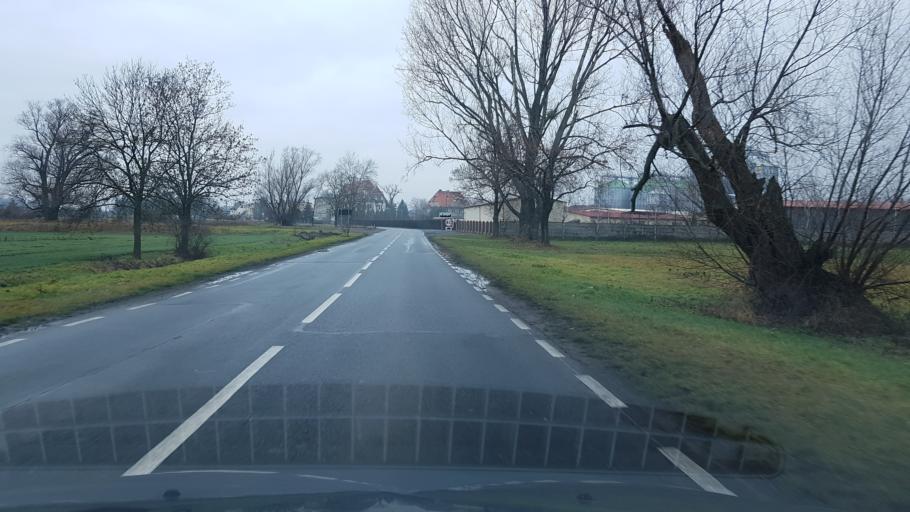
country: PL
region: Lower Silesian Voivodeship
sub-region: Powiat wroclawski
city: Zorawina
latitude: 50.9866
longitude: 17.0171
